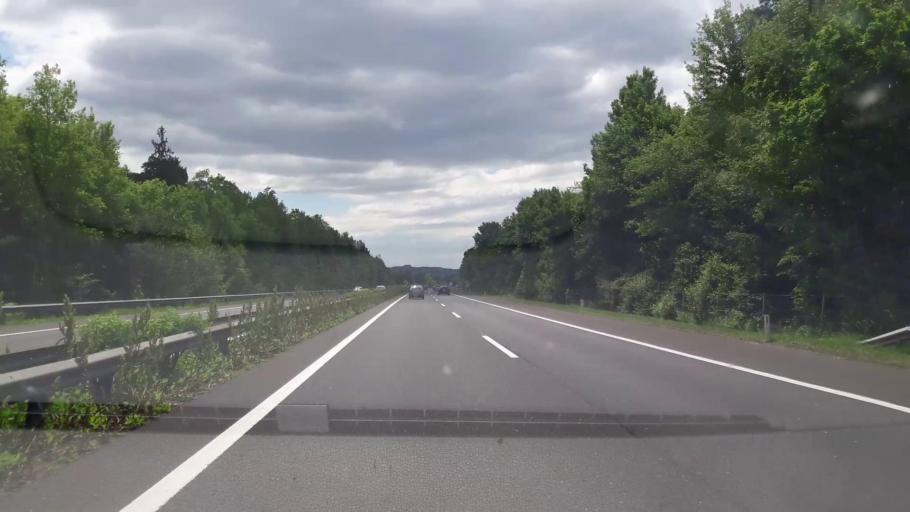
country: AT
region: Styria
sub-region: Politischer Bezirk Hartberg-Fuerstenfeld
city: Hainersdorf
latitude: 47.1087
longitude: 15.9848
